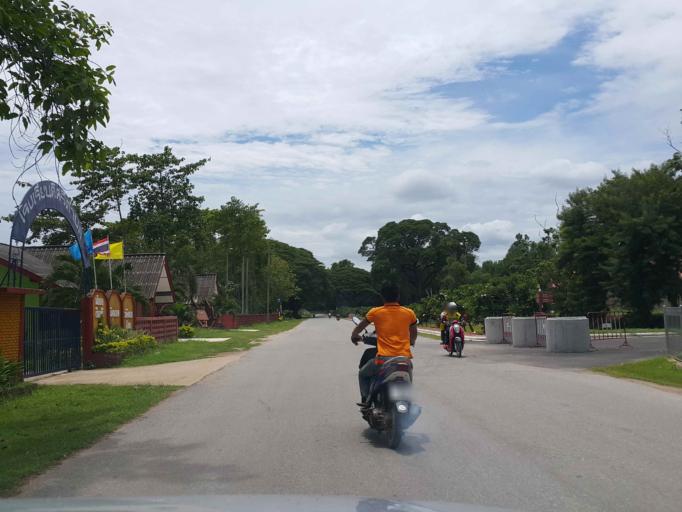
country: TH
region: Sukhothai
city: Ban Na
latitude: 17.0152
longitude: 99.7054
